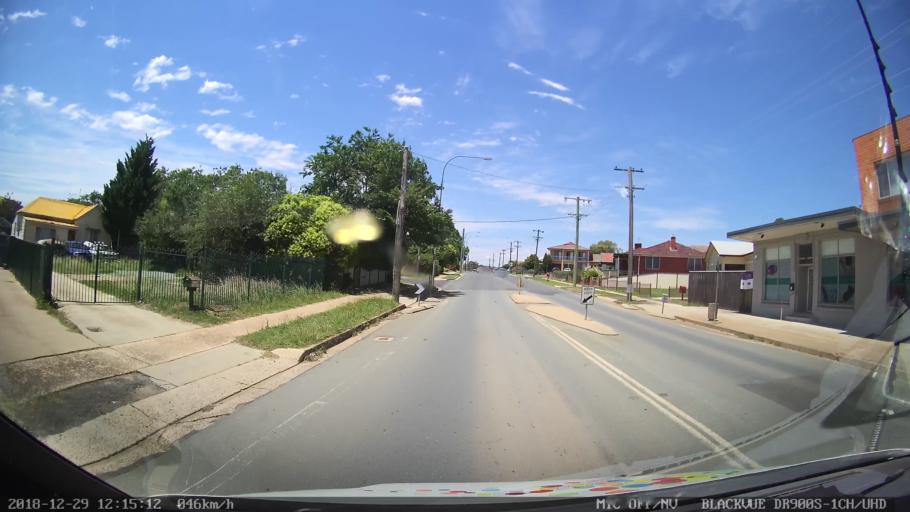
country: AU
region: New South Wales
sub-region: Queanbeyan
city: Queanbeyan
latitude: -35.3602
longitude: 149.2334
